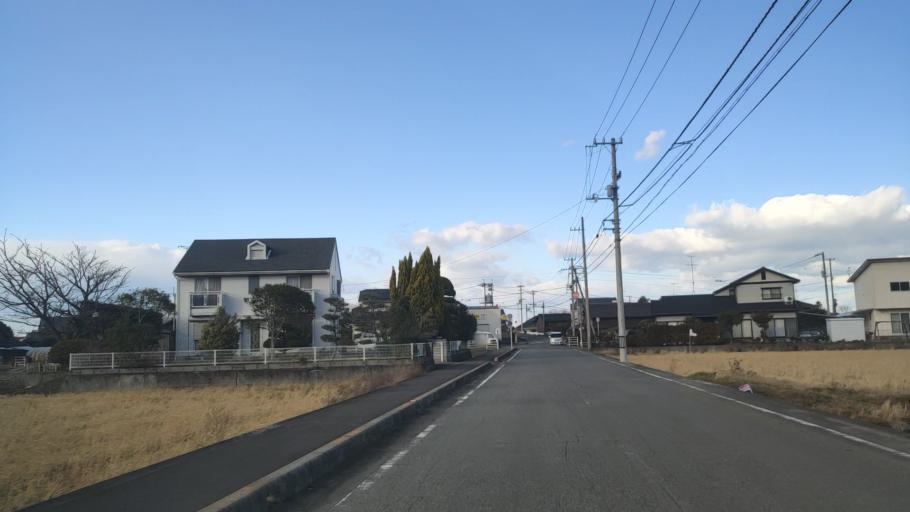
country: JP
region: Ehime
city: Saijo
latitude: 33.9055
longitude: 133.1292
